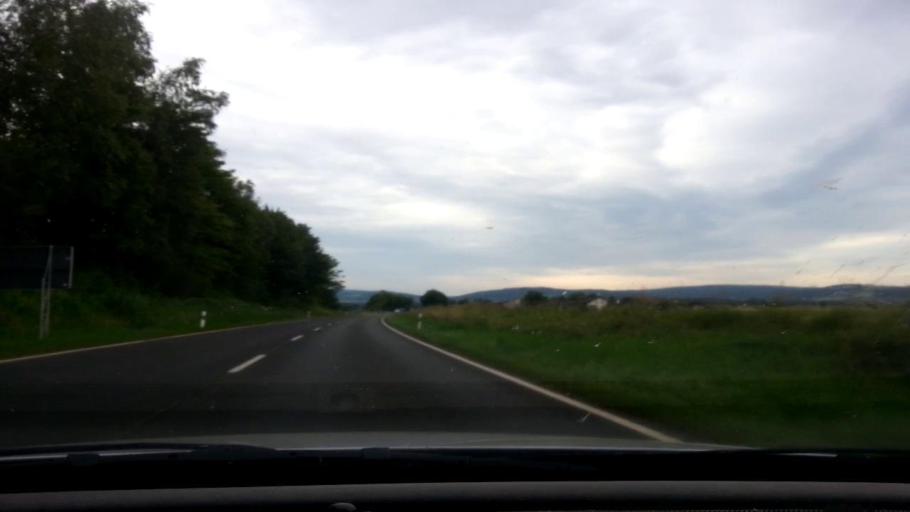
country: DE
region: Bavaria
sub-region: Upper Palatinate
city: Kemnath
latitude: 49.8872
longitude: 11.8827
